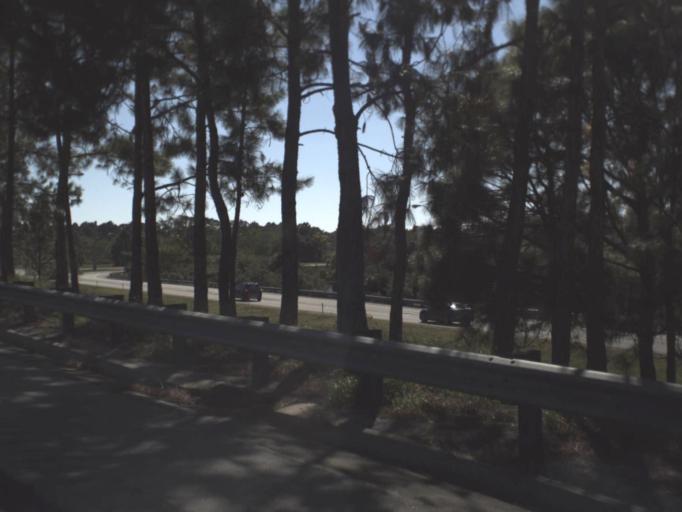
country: US
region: Florida
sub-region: Seminole County
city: Oviedo
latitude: 28.6926
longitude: -81.2289
